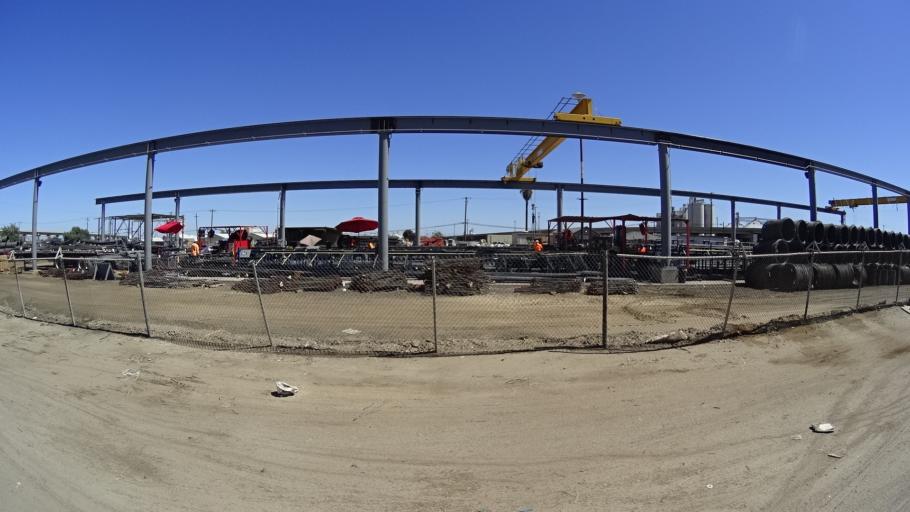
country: US
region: California
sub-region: Fresno County
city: Easton
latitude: 36.6912
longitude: -119.7517
